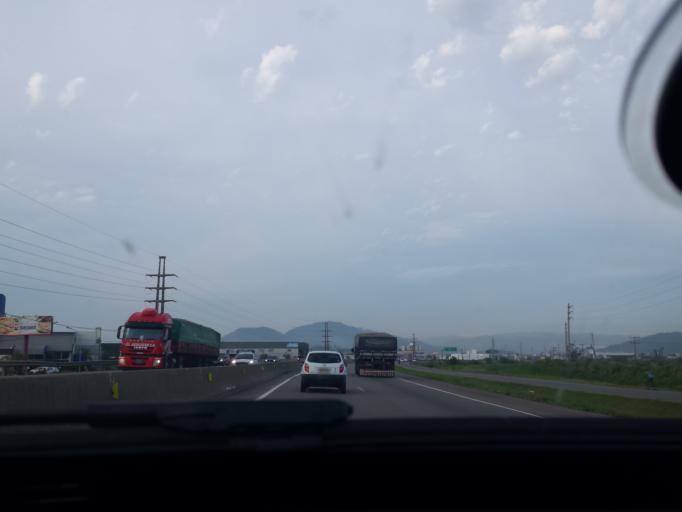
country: BR
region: Santa Catarina
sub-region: Tubarao
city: Tubarao
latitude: -28.4669
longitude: -48.9979
